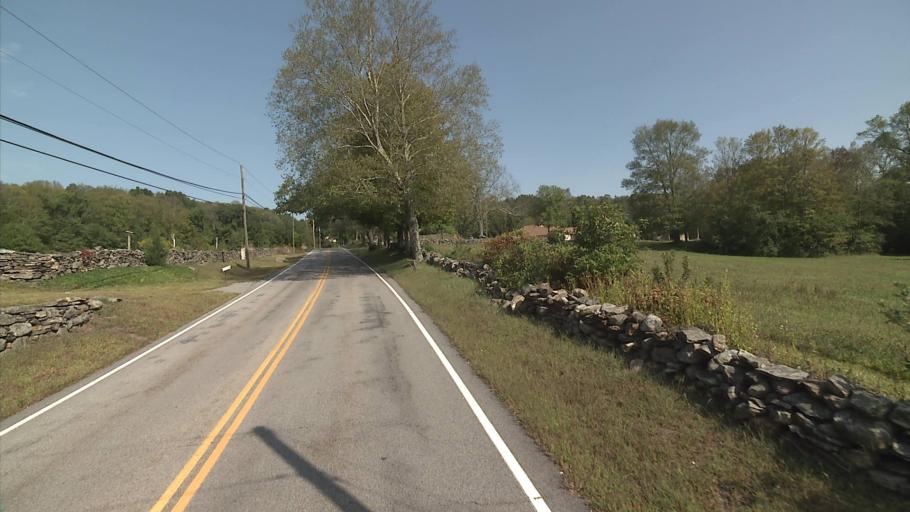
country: US
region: Connecticut
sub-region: Windham County
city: Plainfield Village
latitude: 41.7134
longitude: -71.9702
